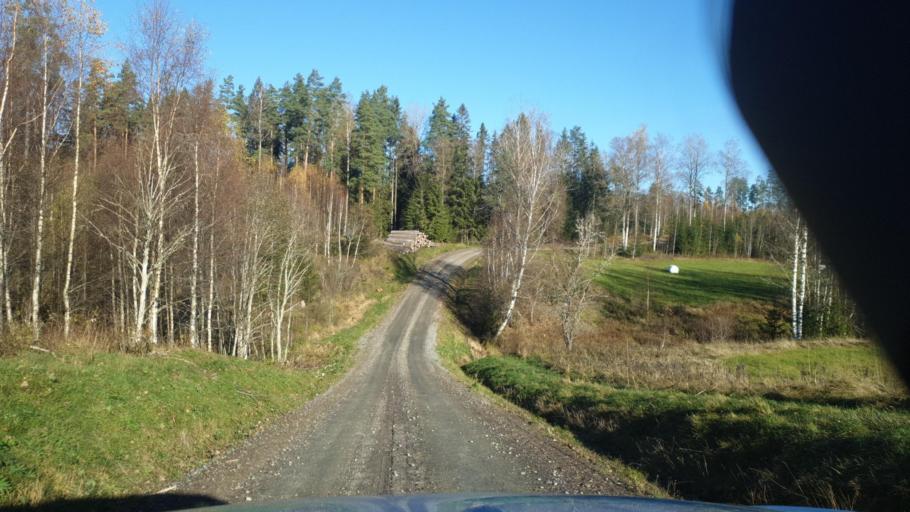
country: SE
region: Vaermland
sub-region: Karlstads Kommun
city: Edsvalla
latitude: 59.4730
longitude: 13.1271
